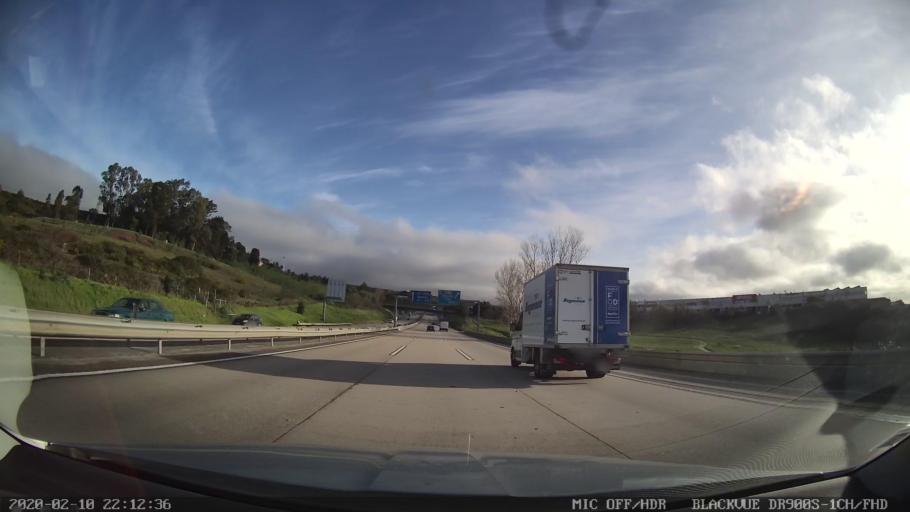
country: PT
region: Lisbon
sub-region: Loures
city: Santo Antao do Tojal
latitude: 38.8621
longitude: -9.1550
